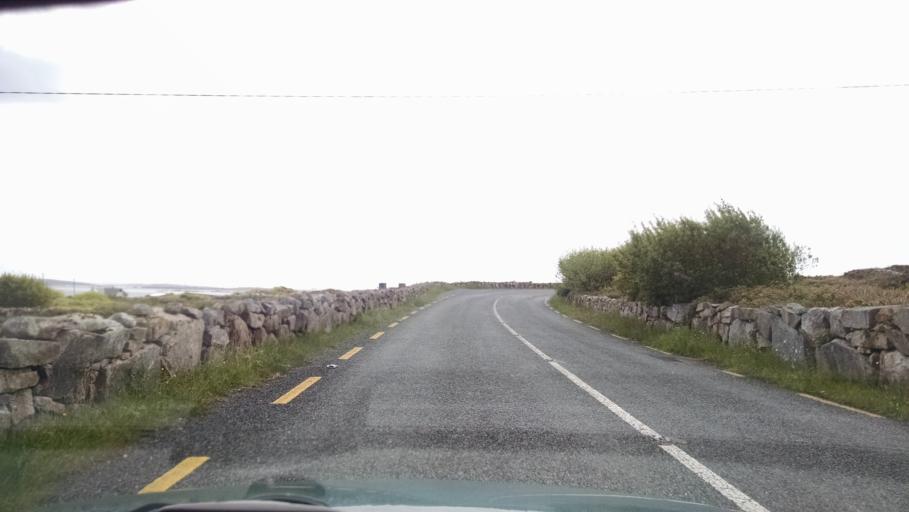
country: IE
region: Connaught
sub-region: County Galway
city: Clifden
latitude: 53.3124
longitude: -9.7330
